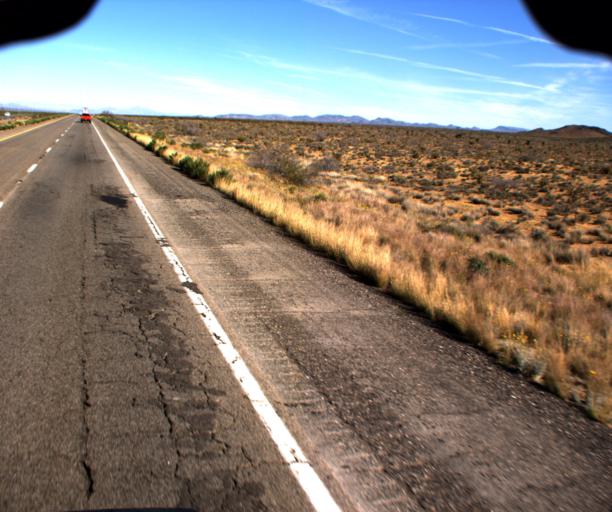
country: US
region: Arizona
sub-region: Mohave County
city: Dolan Springs
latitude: 35.4664
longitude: -114.3085
